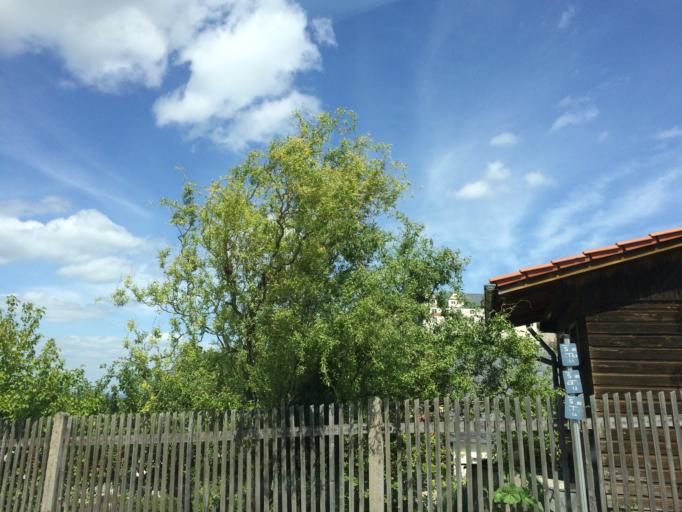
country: DE
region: Thuringia
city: Ranis
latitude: 50.6599
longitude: 11.5635
